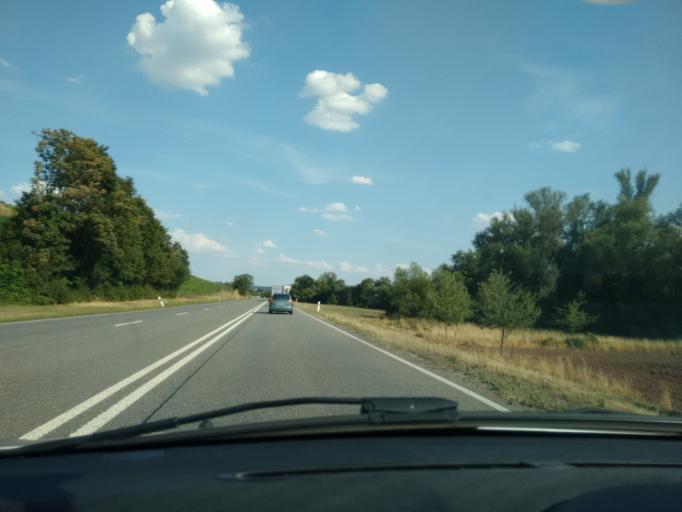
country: DE
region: Rheinland-Pfalz
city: Monzingen
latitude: 49.7976
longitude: 7.5775
